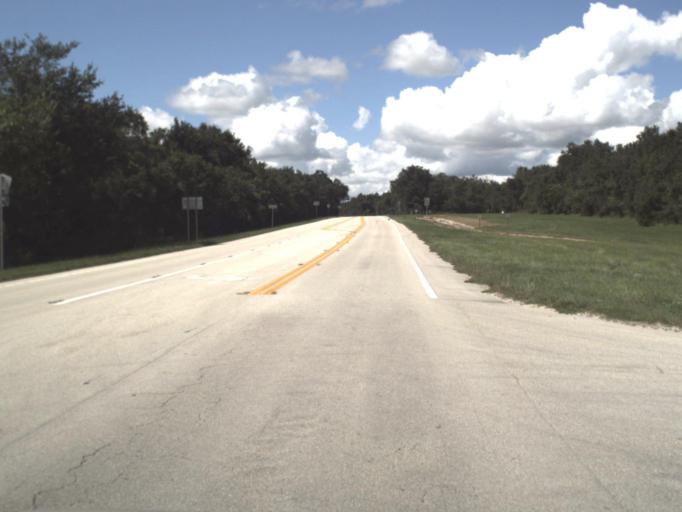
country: US
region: Florida
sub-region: DeSoto County
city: Arcadia
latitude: 27.2279
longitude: -81.8919
